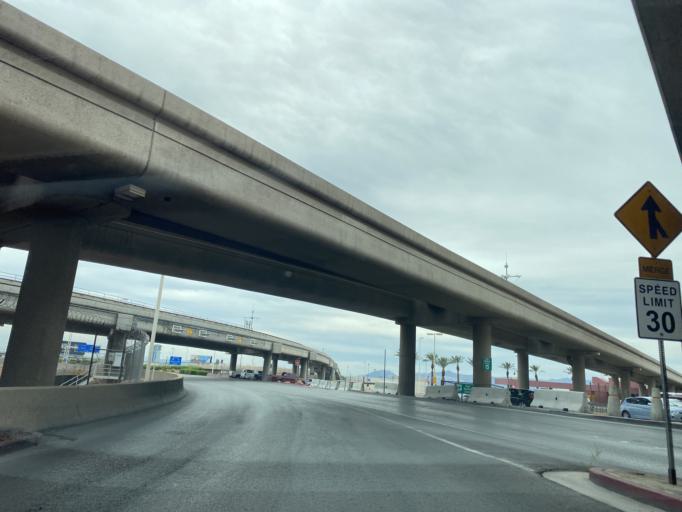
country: US
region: Nevada
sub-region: Clark County
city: Paradise
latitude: 36.0839
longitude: -115.1488
